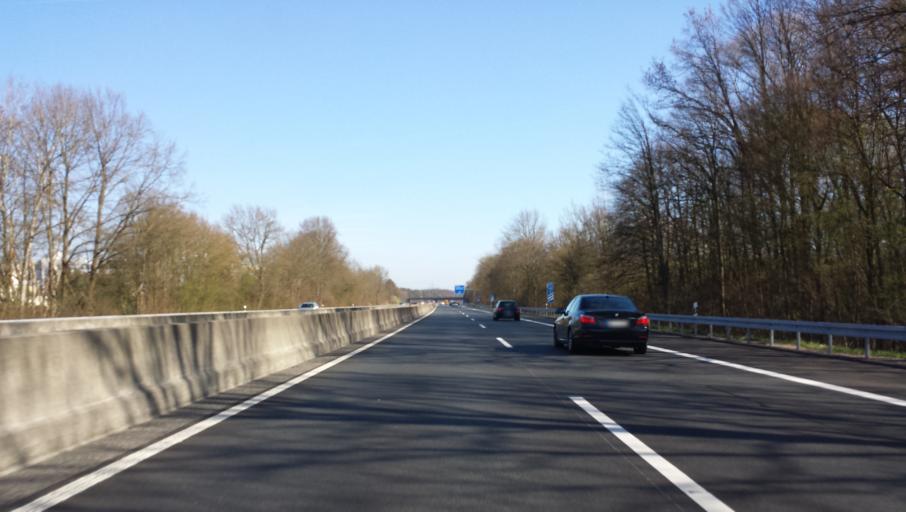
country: DE
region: Hesse
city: Dreieich
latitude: 50.0247
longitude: 8.7105
